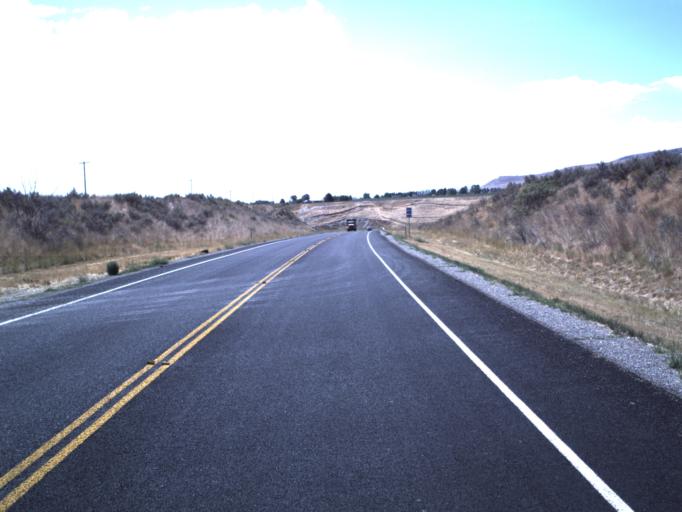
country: US
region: Utah
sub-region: Box Elder County
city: Garland
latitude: 41.8448
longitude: -112.1465
